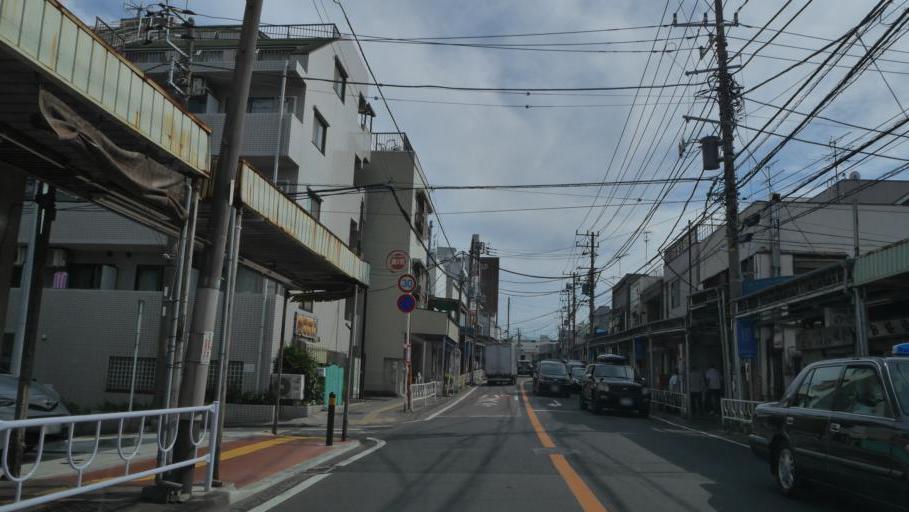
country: JP
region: Kanagawa
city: Yokohama
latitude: 35.4317
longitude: 139.6377
